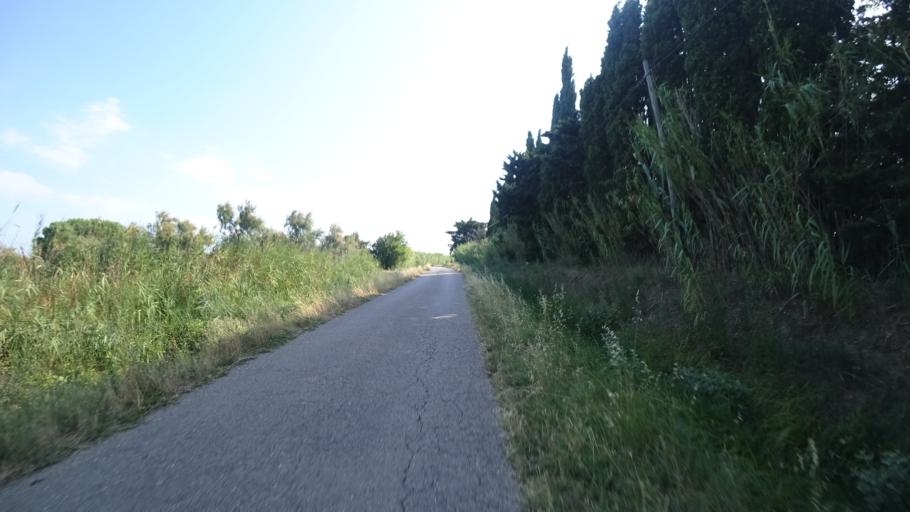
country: FR
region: Languedoc-Roussillon
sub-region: Departement des Pyrenees-Orientales
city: Saint-Laurent-de-la-Salanque
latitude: 42.7845
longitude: 3.0011
